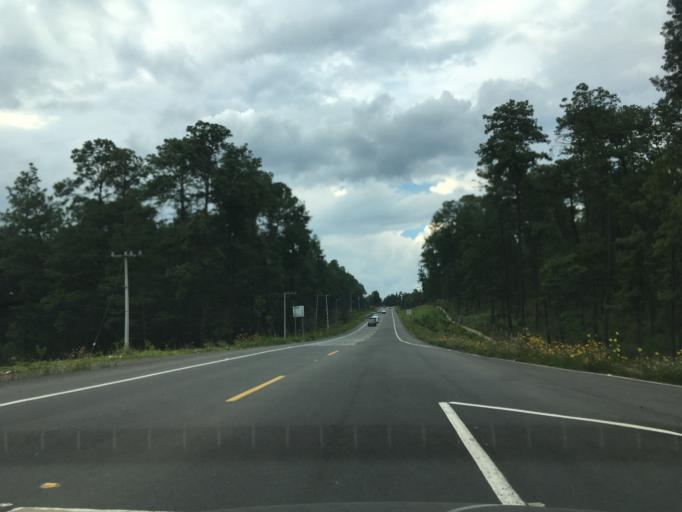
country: MX
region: Michoacan
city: Angahuan
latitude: 19.5192
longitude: -102.1786
